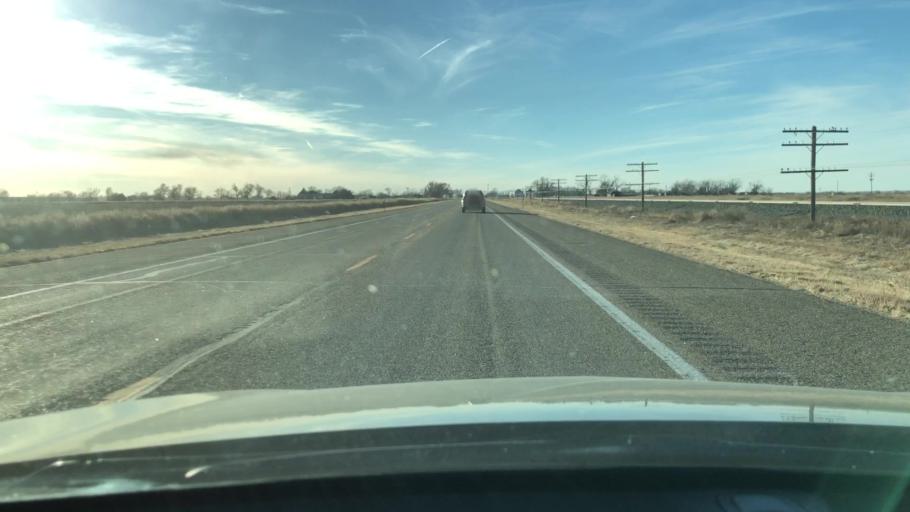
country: US
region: Colorado
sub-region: Prowers County
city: Lamar
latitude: 38.0834
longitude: -102.4036
